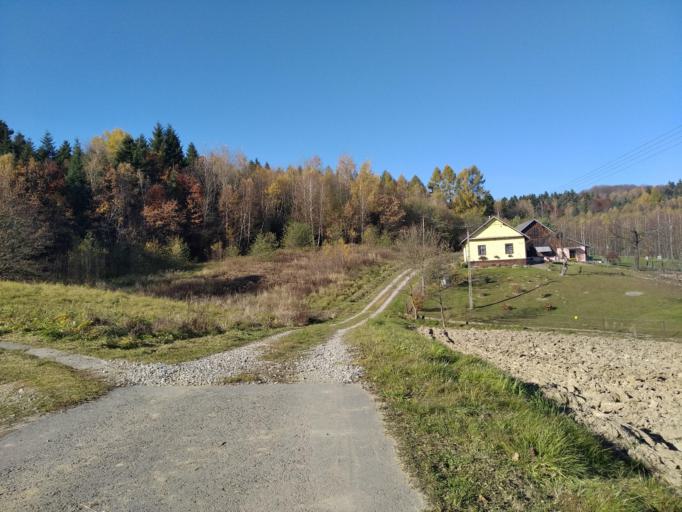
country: PL
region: Subcarpathian Voivodeship
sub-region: Powiat strzyzowski
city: Frysztak
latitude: 49.8509
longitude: 21.6020
